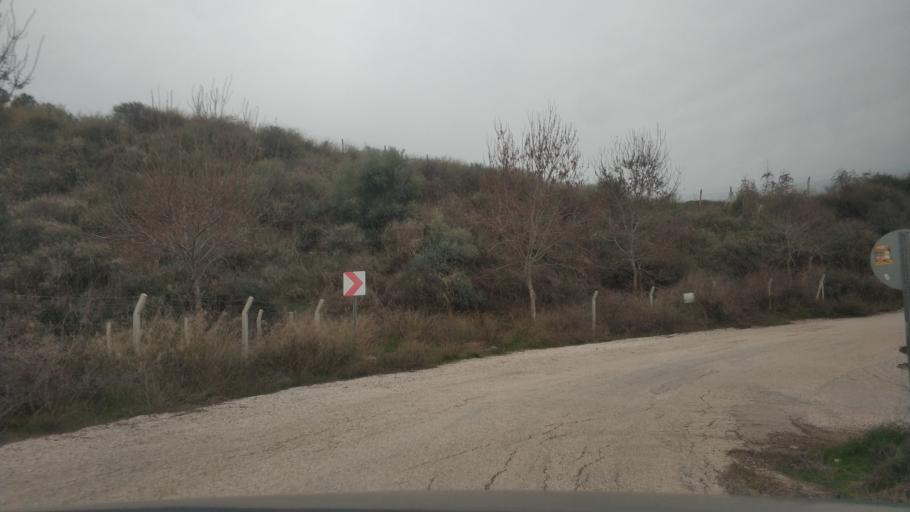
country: TR
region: Adana
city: Adana
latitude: 37.0763
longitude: 35.3209
